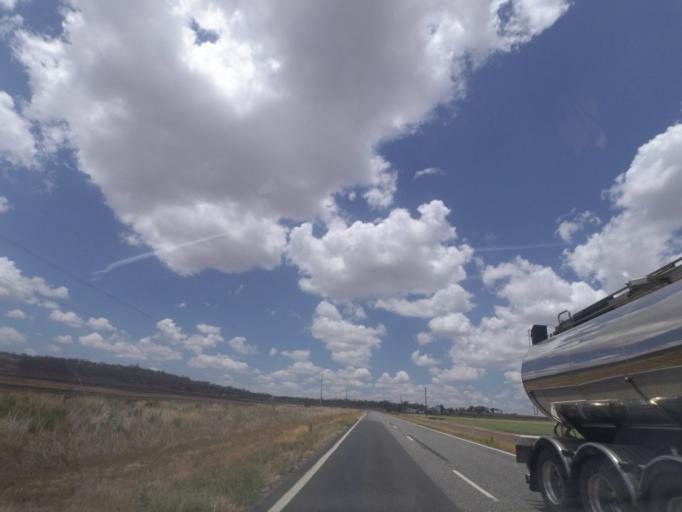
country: AU
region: Queensland
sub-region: Toowoomba
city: Top Camp
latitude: -27.8743
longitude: 151.9645
